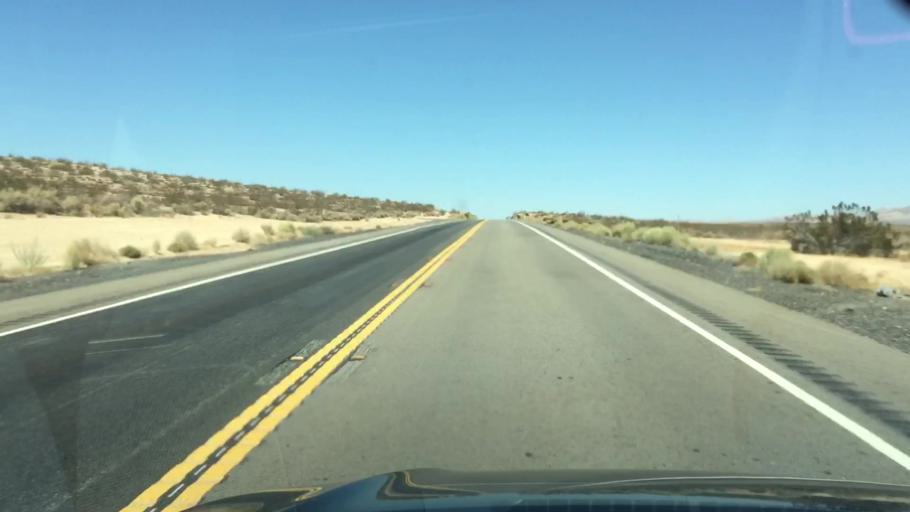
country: US
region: California
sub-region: Kern County
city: Boron
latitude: 35.0640
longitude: -117.5600
